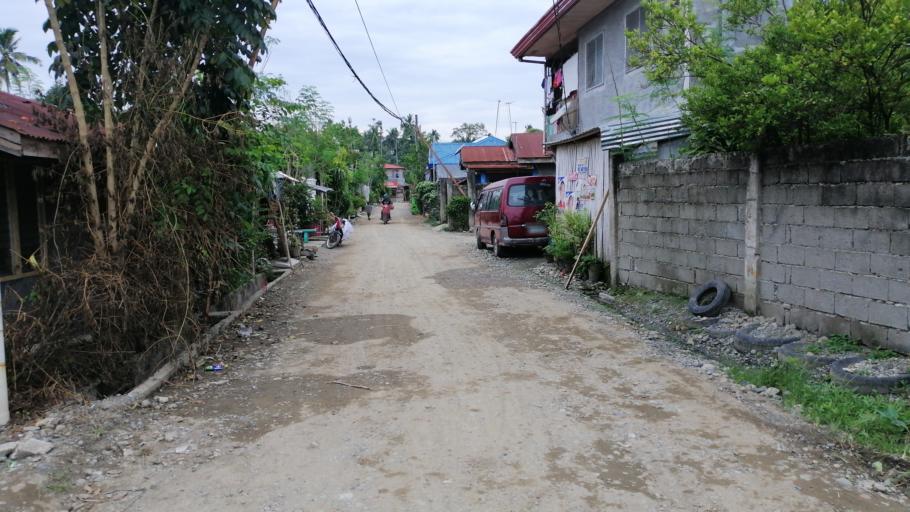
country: PH
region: Davao
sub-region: Province of Davao del Norte
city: Tagum
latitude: 7.4499
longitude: 125.8200
